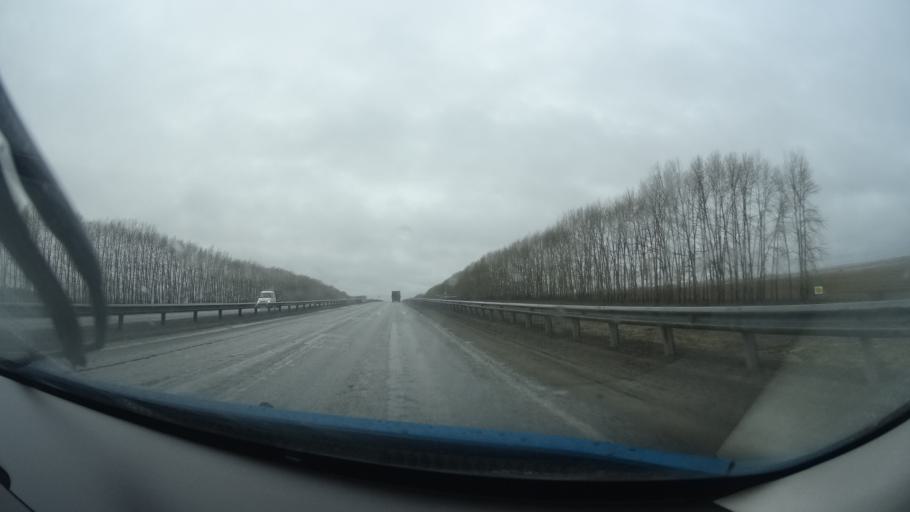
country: RU
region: Bashkortostan
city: Dmitriyevka
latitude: 54.7129
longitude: 55.2090
